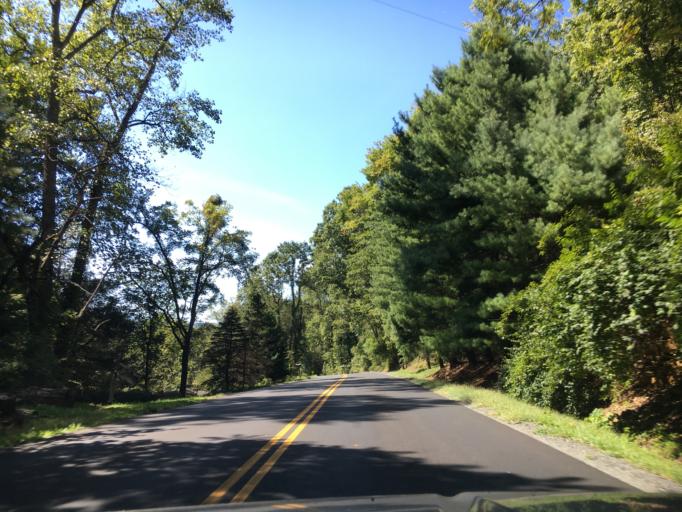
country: US
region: Virginia
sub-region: Albemarle County
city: Crozet
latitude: 37.9796
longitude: -78.6978
